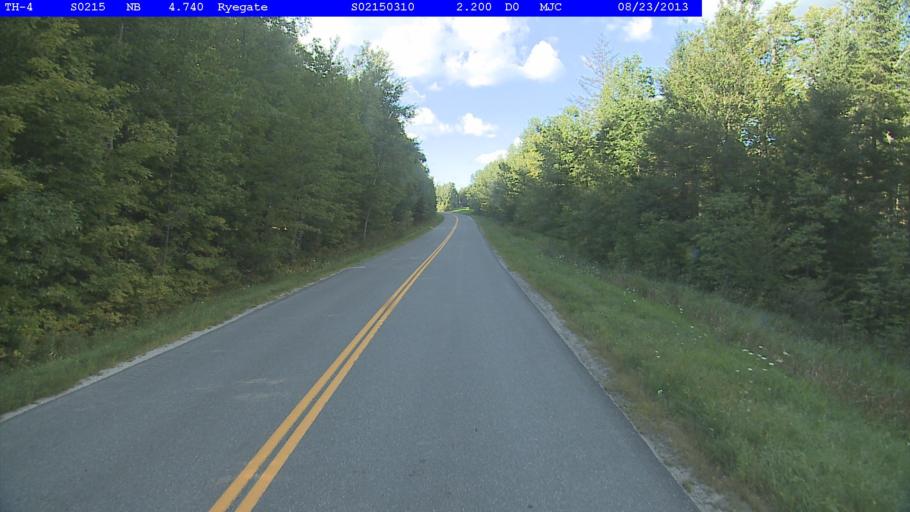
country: US
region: New Hampshire
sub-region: Grafton County
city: Woodsville
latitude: 44.2726
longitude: -72.1738
